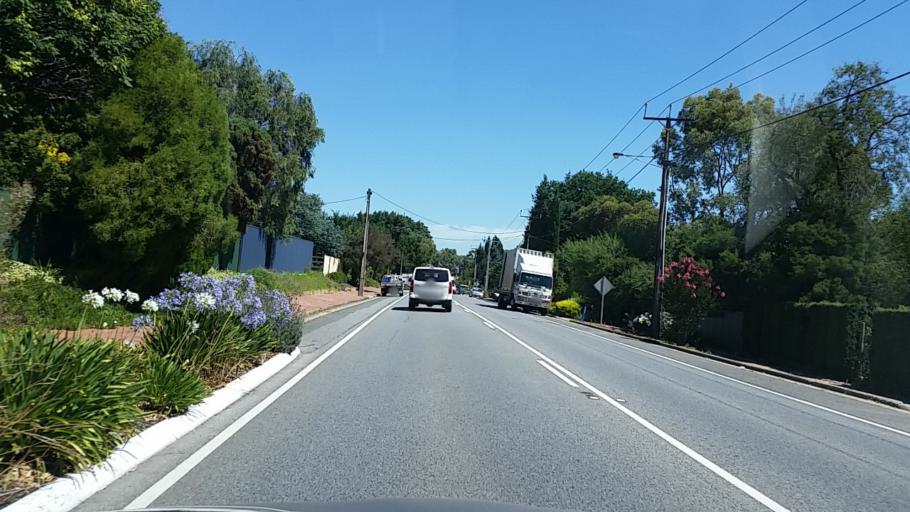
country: AU
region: South Australia
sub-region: Mount Barker
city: Little Hampton
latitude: -35.0504
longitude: 138.8587
